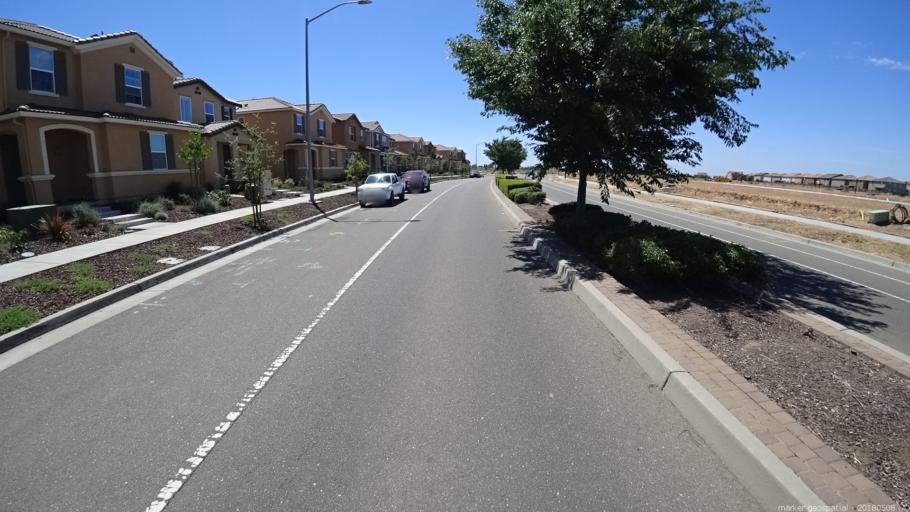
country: US
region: California
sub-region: Sacramento County
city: Elverta
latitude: 38.6706
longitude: -121.5287
